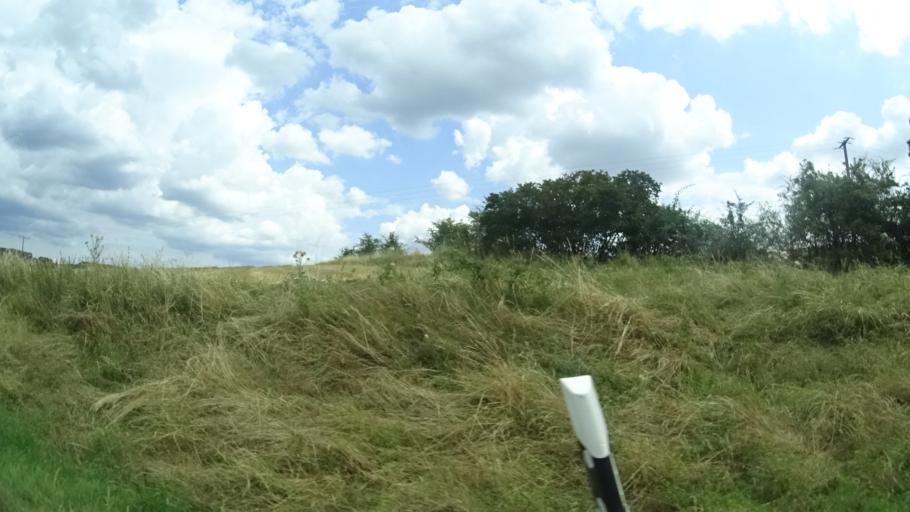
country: DE
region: Hesse
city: Gedern
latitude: 50.4077
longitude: 9.1951
